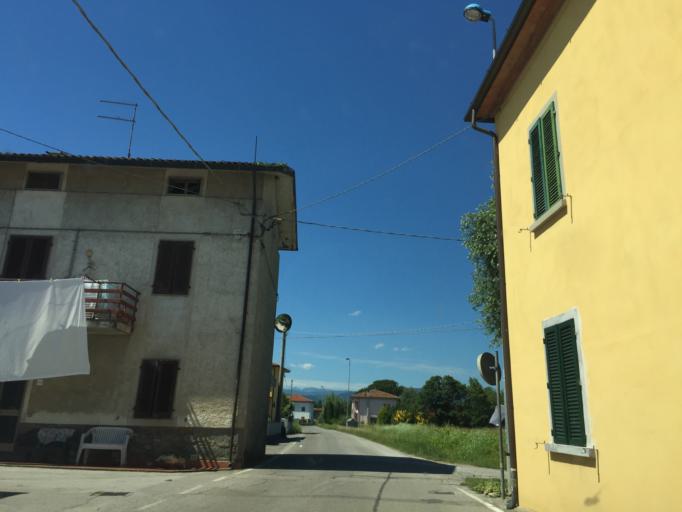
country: IT
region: Tuscany
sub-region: Provincia di Pistoia
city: Anchione
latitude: 43.8259
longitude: 10.7587
